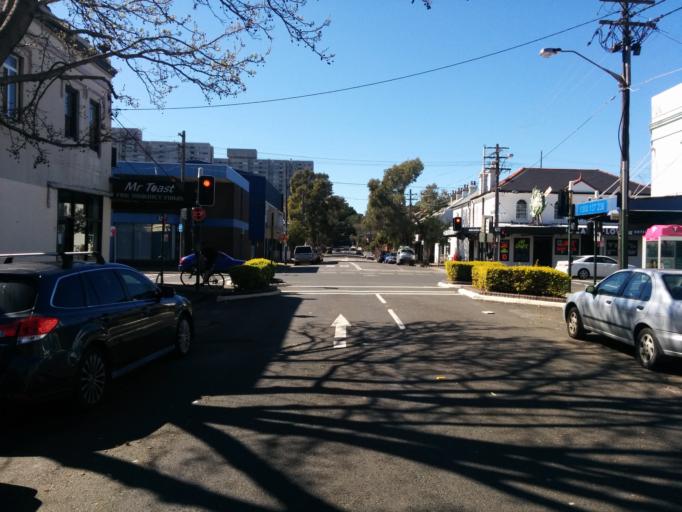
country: AU
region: New South Wales
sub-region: City of Sydney
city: Alexandria
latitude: -33.8988
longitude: 151.1996
